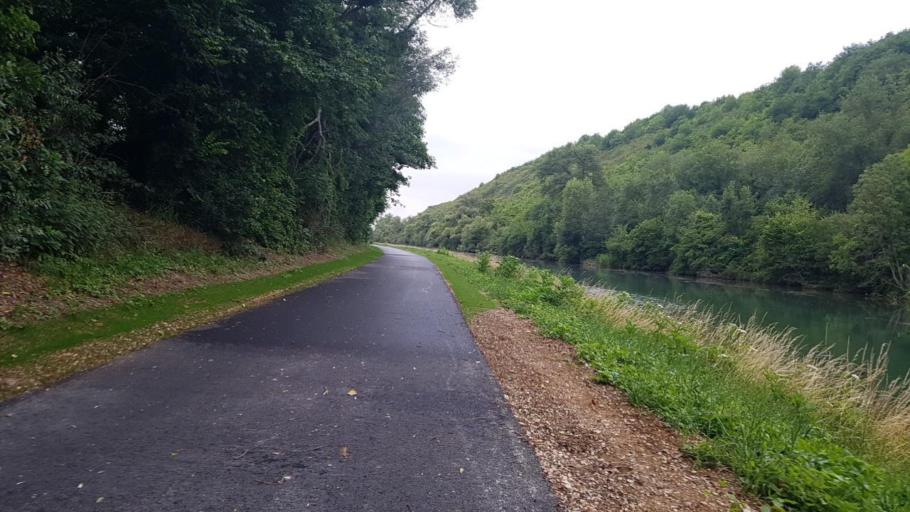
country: FR
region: Champagne-Ardenne
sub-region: Departement de la Marne
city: Vitry-le-Francois
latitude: 48.7688
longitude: 4.5566
